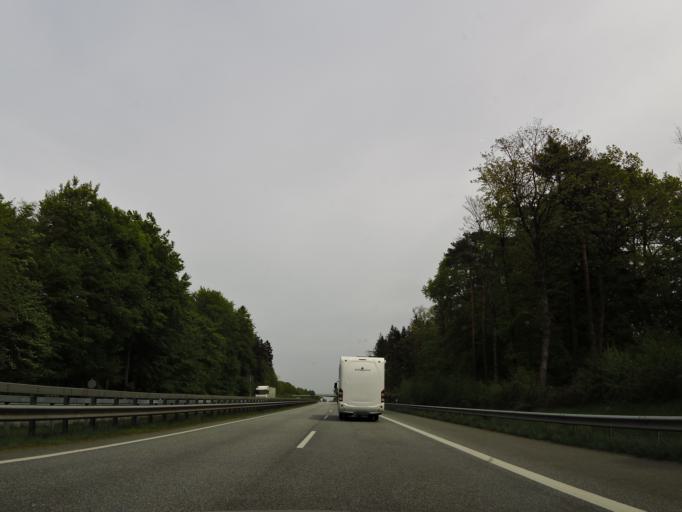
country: DE
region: Schleswig-Holstein
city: Heiligenstedten
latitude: 53.9433
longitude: 9.4869
